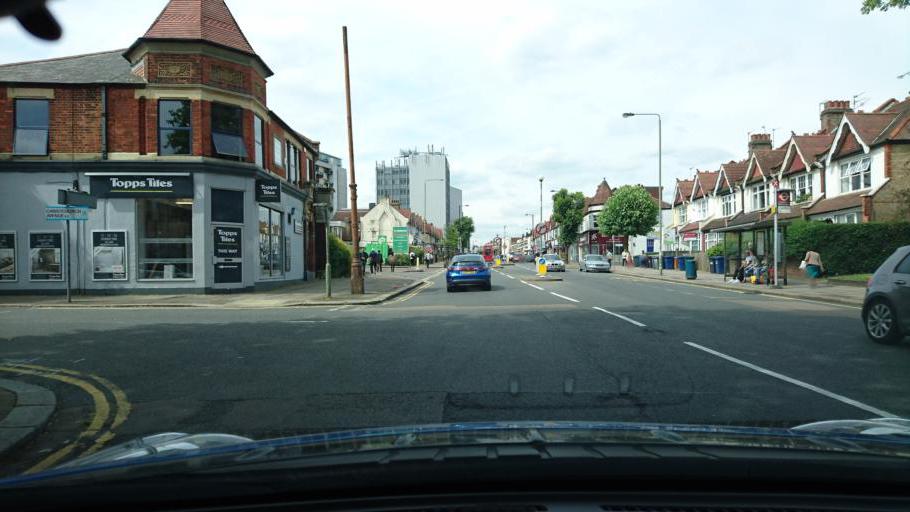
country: GB
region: England
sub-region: Greater London
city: Hendon
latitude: 51.6107
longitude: -0.1755
